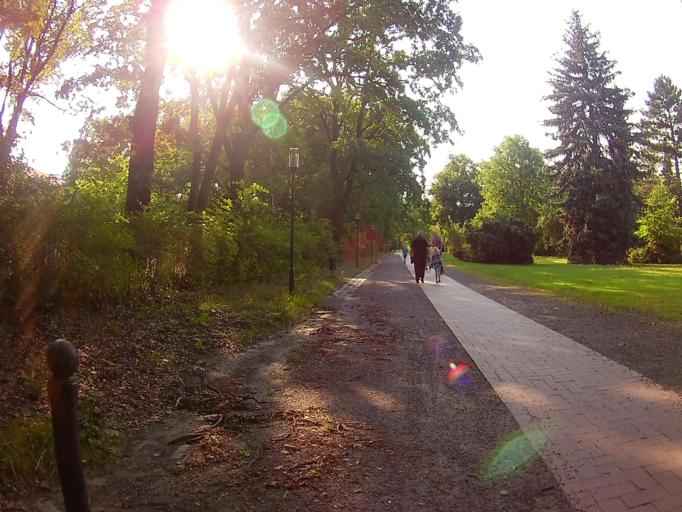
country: DE
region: Berlin
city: Biesdorf
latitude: 52.5148
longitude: 13.5688
